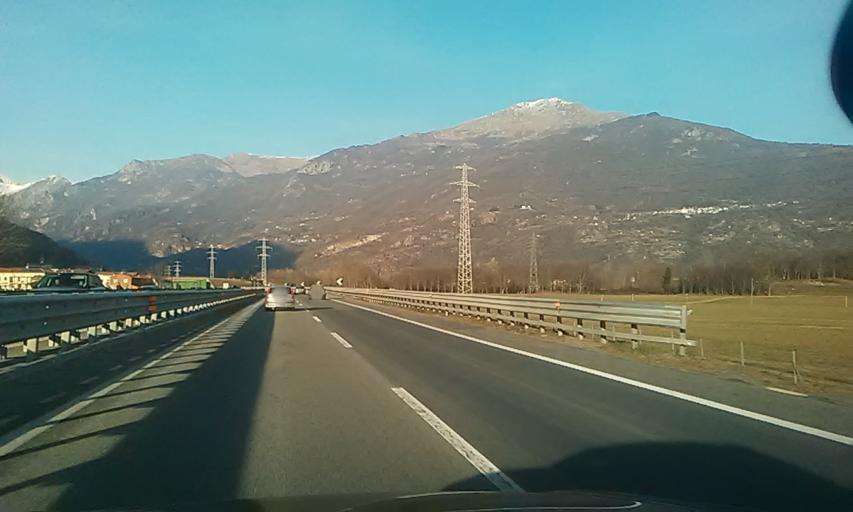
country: IT
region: Piedmont
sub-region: Provincia di Torino
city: Quassolo
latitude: 45.5158
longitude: 7.8345
